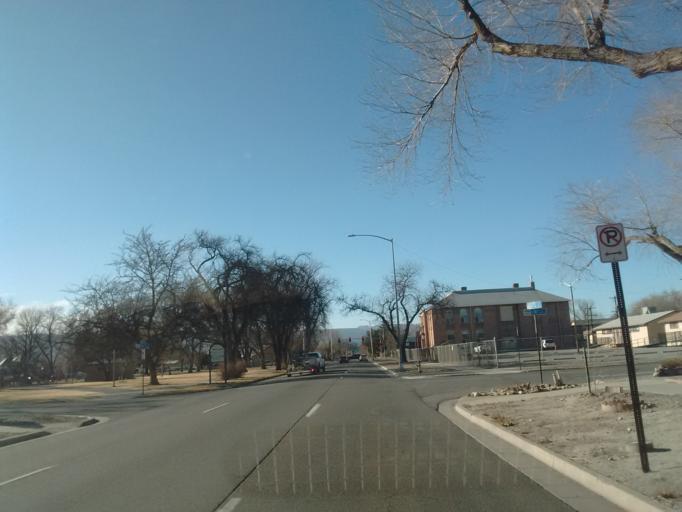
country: US
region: Colorado
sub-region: Mesa County
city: Grand Junction
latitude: 39.0654
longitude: -108.5558
